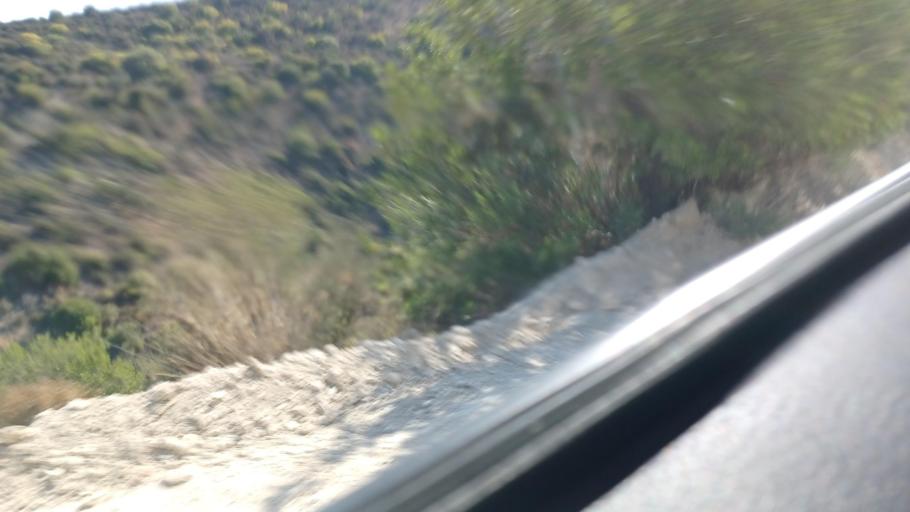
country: CY
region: Pafos
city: Tala
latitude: 34.8657
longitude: 32.4410
